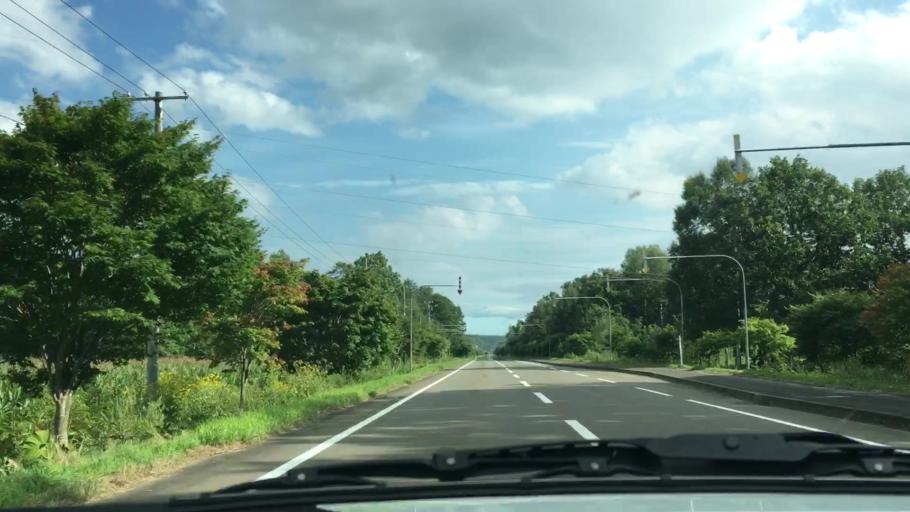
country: JP
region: Hokkaido
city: Otofuke
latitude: 43.3197
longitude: 143.3028
